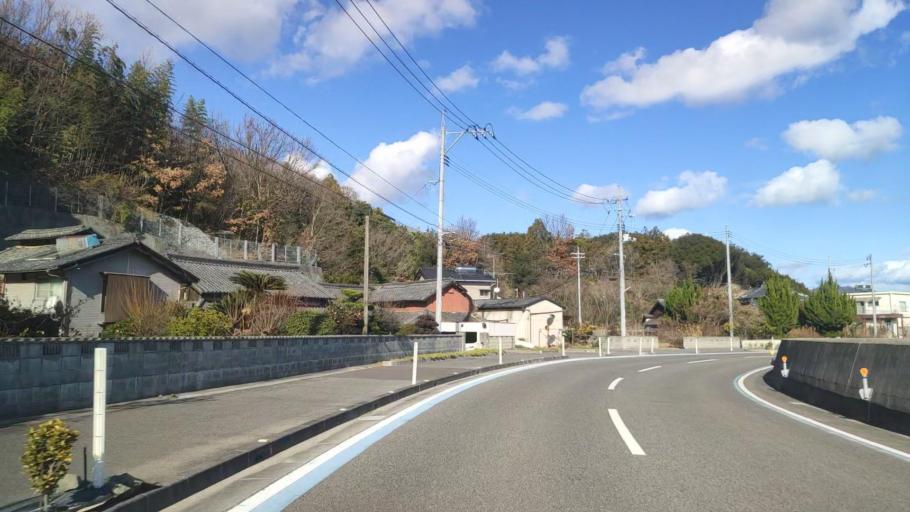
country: JP
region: Hiroshima
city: Innoshima
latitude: 34.2217
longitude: 133.1074
